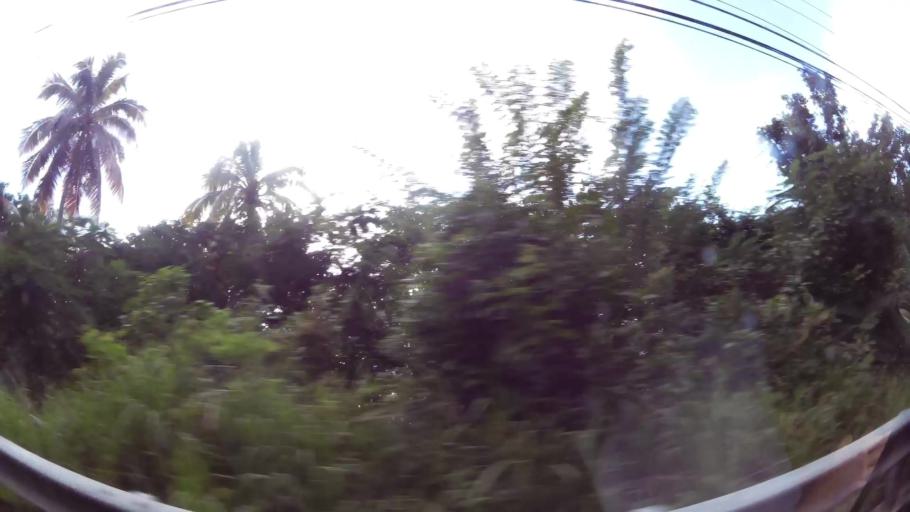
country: DM
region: Saint Paul
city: Mahaut
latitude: 15.3531
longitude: -61.3932
